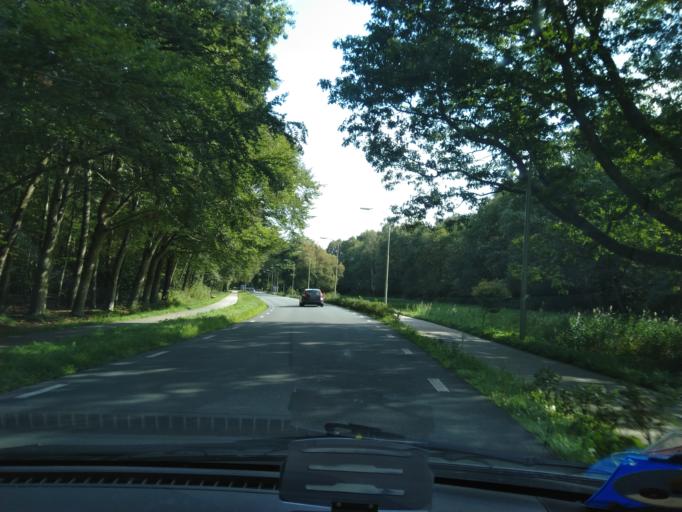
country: NL
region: Groningen
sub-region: Gemeente Haren
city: Haren
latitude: 53.1634
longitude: 6.5558
